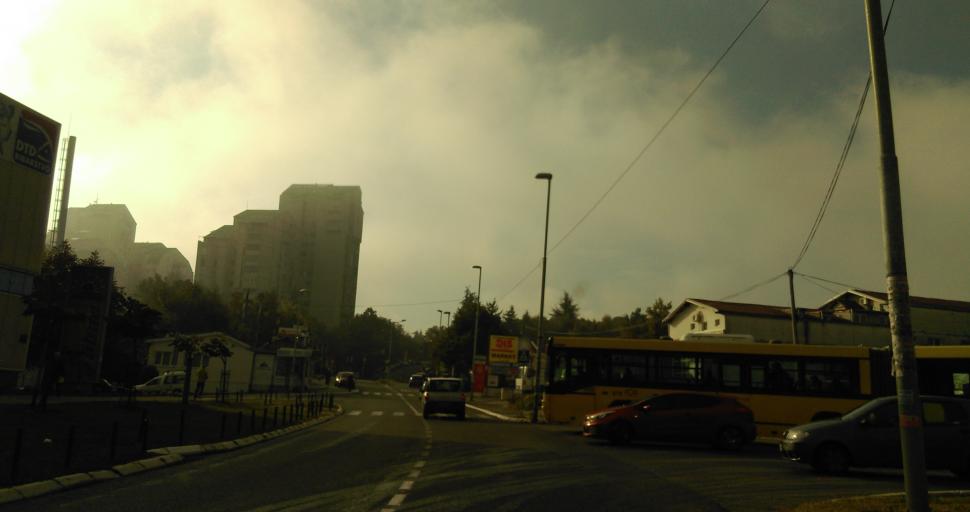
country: RS
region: Central Serbia
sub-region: Belgrade
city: Rakovica
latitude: 44.7319
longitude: 20.4207
